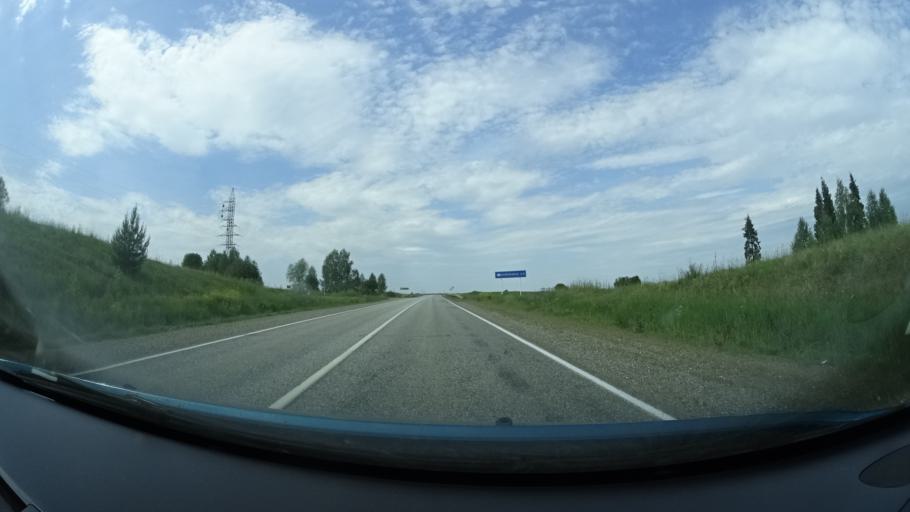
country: RU
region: Perm
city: Barda
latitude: 57.0927
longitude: 55.5354
